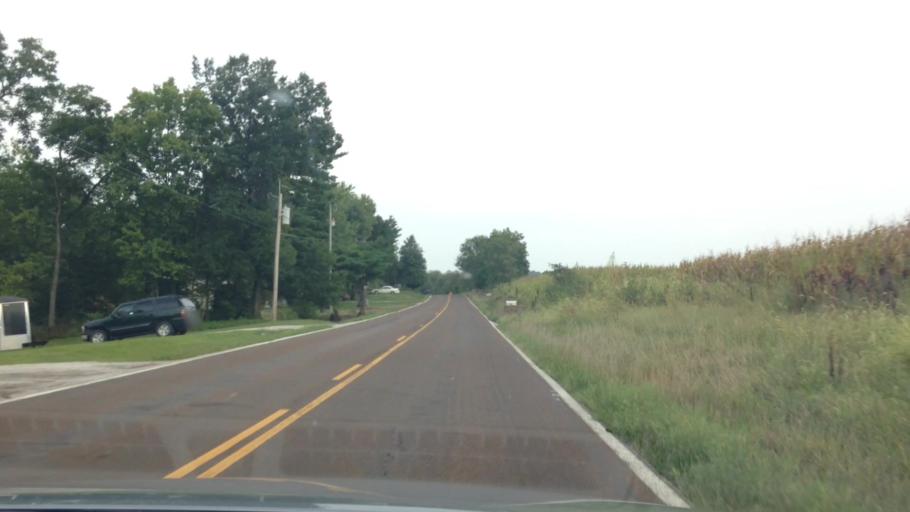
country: US
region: Missouri
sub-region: Clay County
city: Smithville
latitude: 39.4020
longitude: -94.5896
